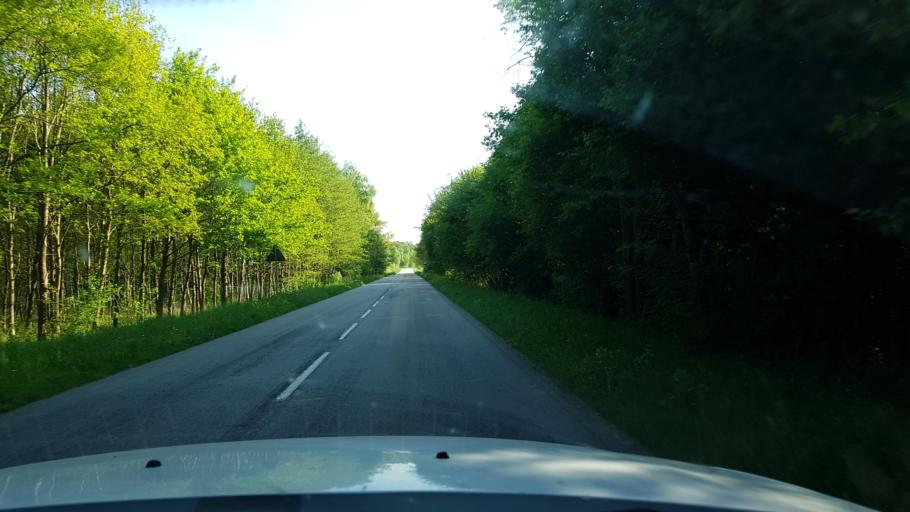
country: PL
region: West Pomeranian Voivodeship
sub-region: Powiat lobeski
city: Resko
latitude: 53.7540
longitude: 15.3761
